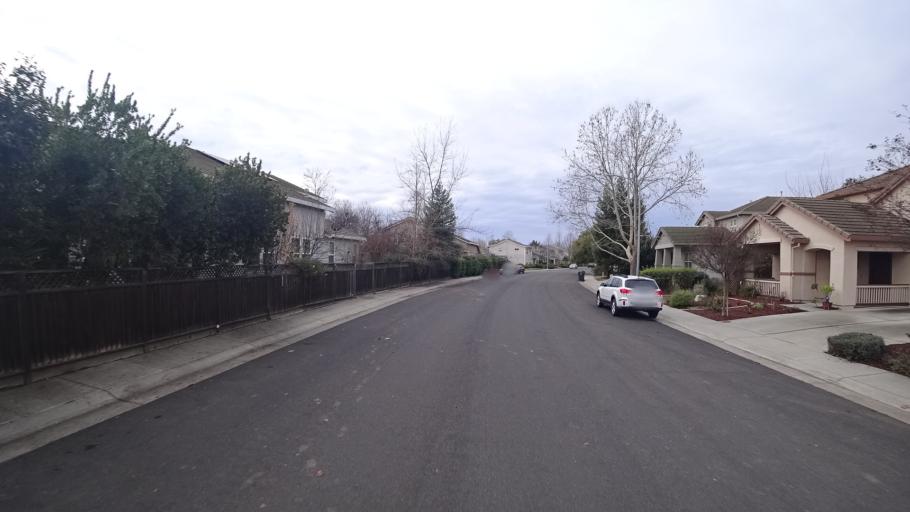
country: US
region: California
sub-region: Yolo County
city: Davis
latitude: 38.5678
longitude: -121.7230
